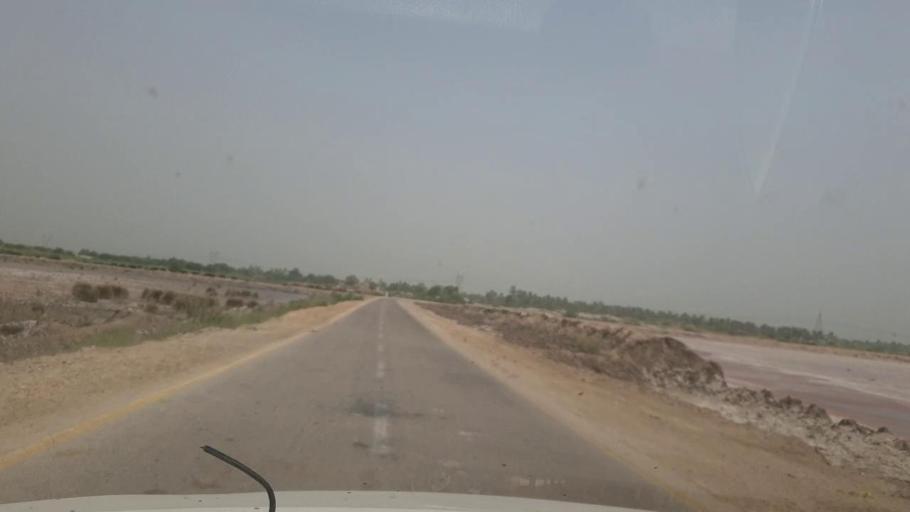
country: PK
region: Sindh
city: Kot Diji
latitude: 27.4022
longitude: 68.6592
